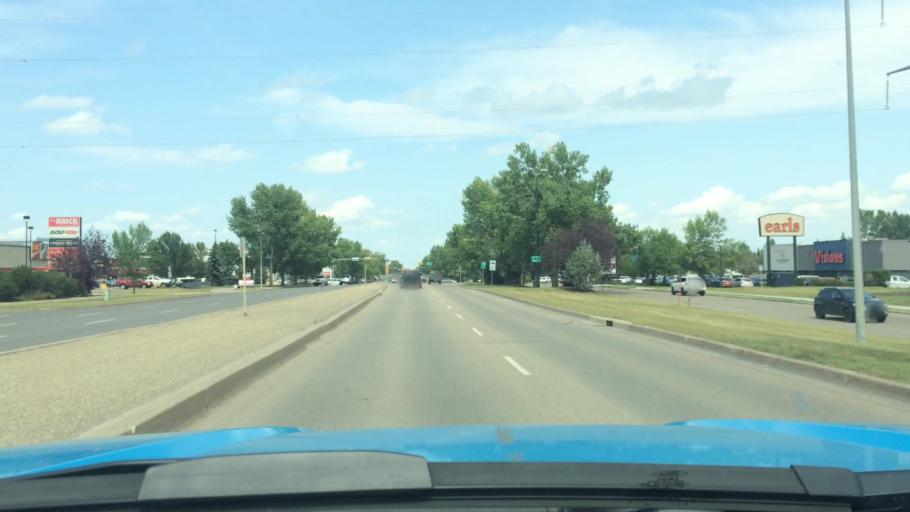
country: CA
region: Alberta
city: Red Deer
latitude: 52.2368
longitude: -113.8139
